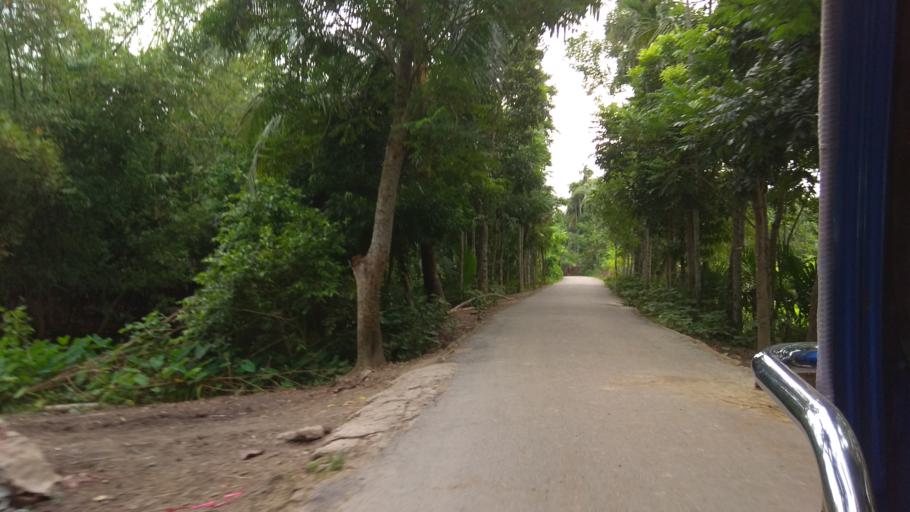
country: BD
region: Khulna
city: Kalia
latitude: 23.0383
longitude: 89.6607
